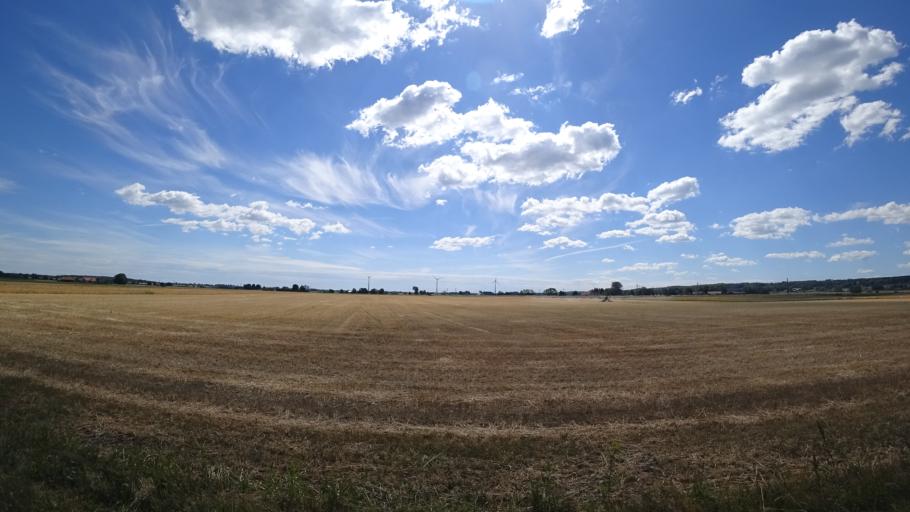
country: SE
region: Skane
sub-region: Kristianstads Kommun
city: Onnestad
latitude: 56.0594
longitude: 14.0363
